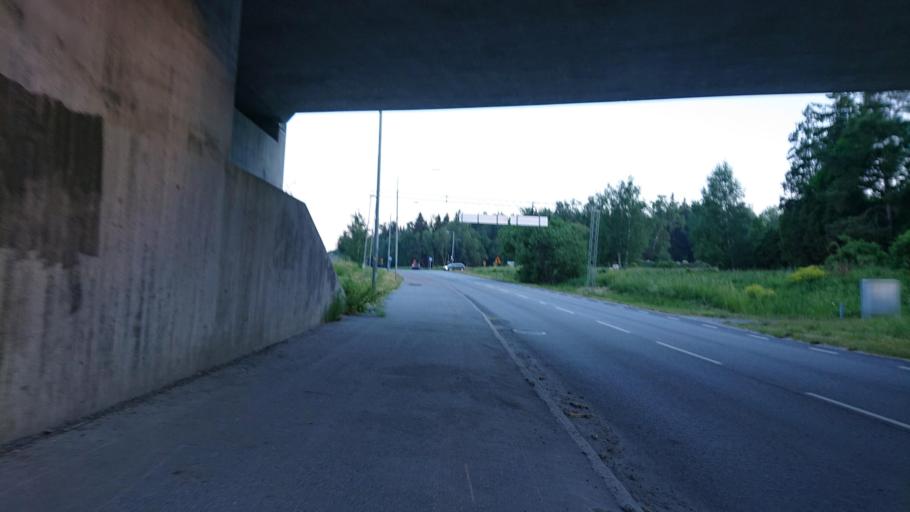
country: SE
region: Stockholm
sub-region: Osterakers Kommun
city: Akersberga
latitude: 59.4804
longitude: 18.2749
